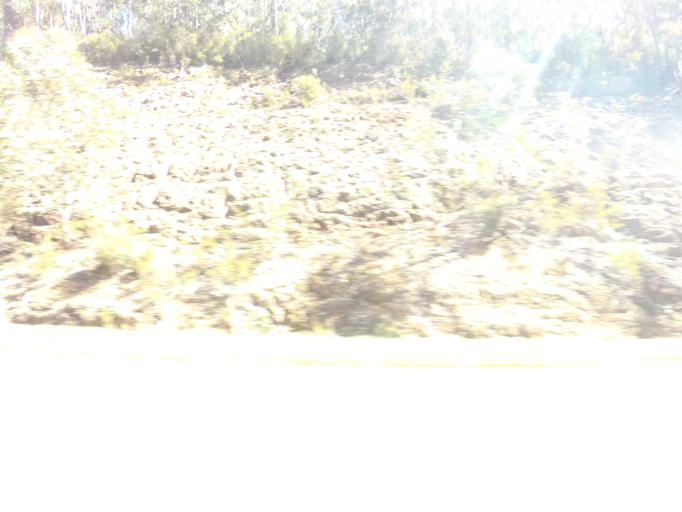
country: AU
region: Tasmania
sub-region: Derwent Valley
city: New Norfolk
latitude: -42.7423
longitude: 146.4984
